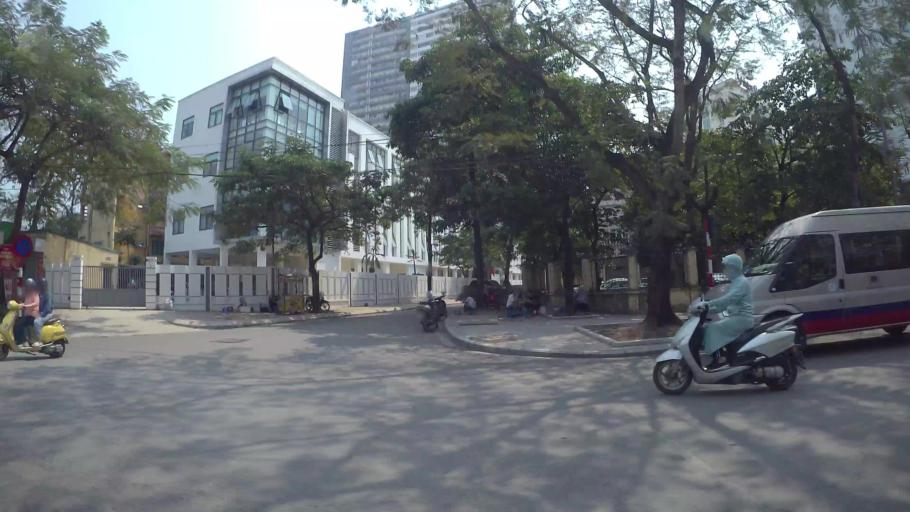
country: VN
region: Ha Noi
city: Thanh Xuan
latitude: 21.0041
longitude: 105.8060
